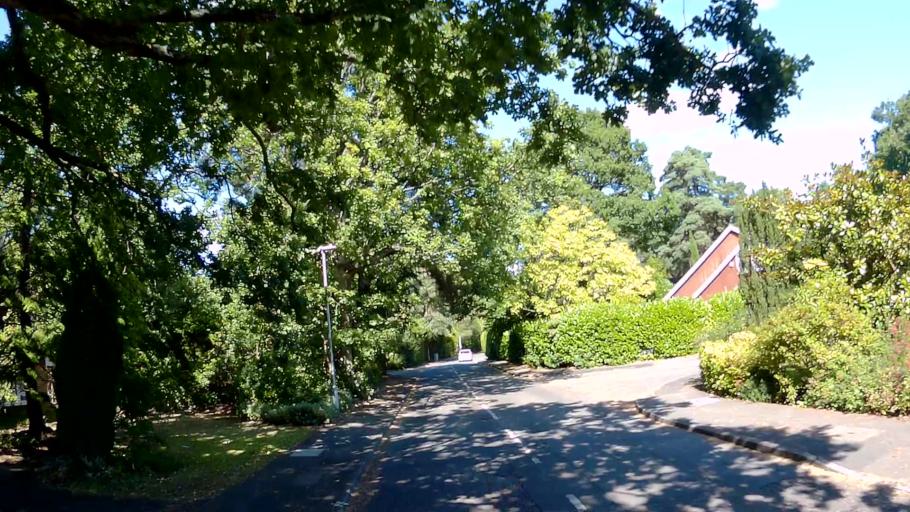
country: GB
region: England
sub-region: Bracknell Forest
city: Crowthorne
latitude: 51.3714
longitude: -0.8079
